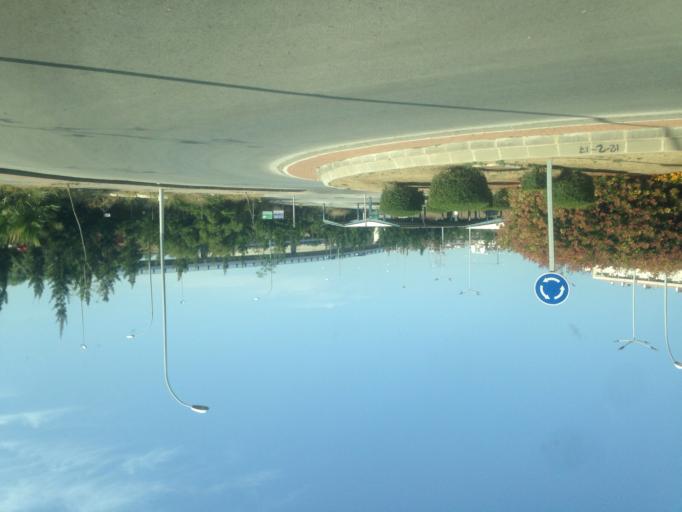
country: ES
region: Andalusia
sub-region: Provincia de Malaga
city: Malaga
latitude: 36.7099
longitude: -4.4590
